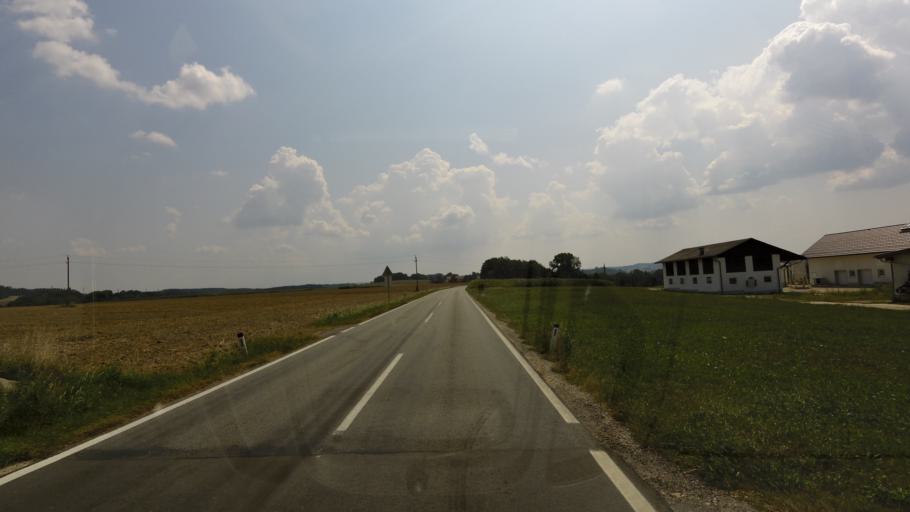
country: AT
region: Upper Austria
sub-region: Politischer Bezirk Ried im Innkreis
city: Waldzell
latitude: 48.1770
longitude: 13.4063
